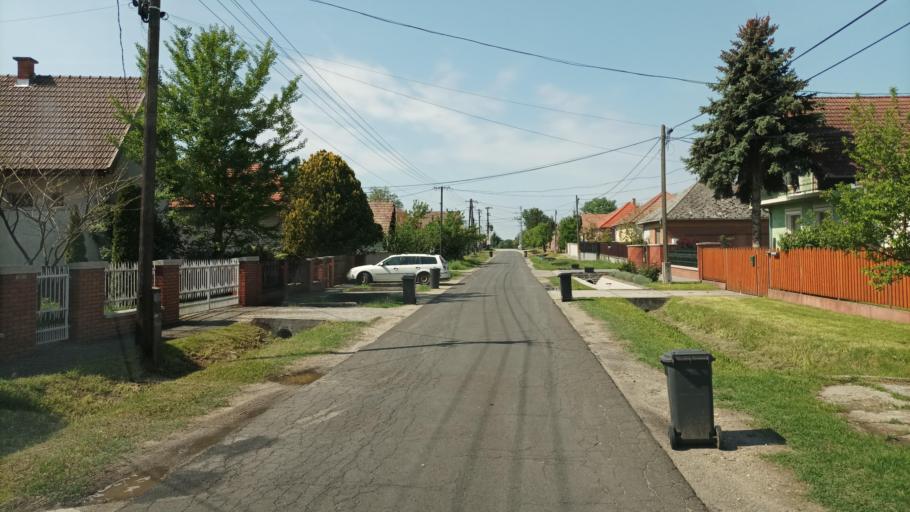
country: HU
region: Pest
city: Tapiosag
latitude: 47.4064
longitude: 19.6280
